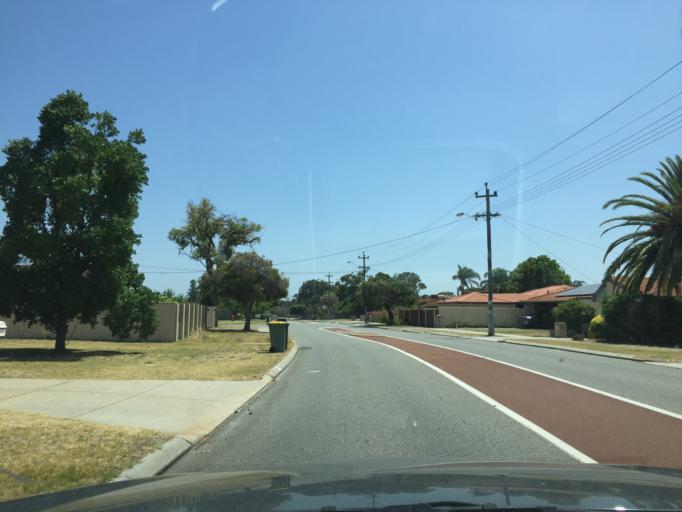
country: AU
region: Western Australia
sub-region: Canning
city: Ferndale
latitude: -32.0409
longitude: 115.9139
